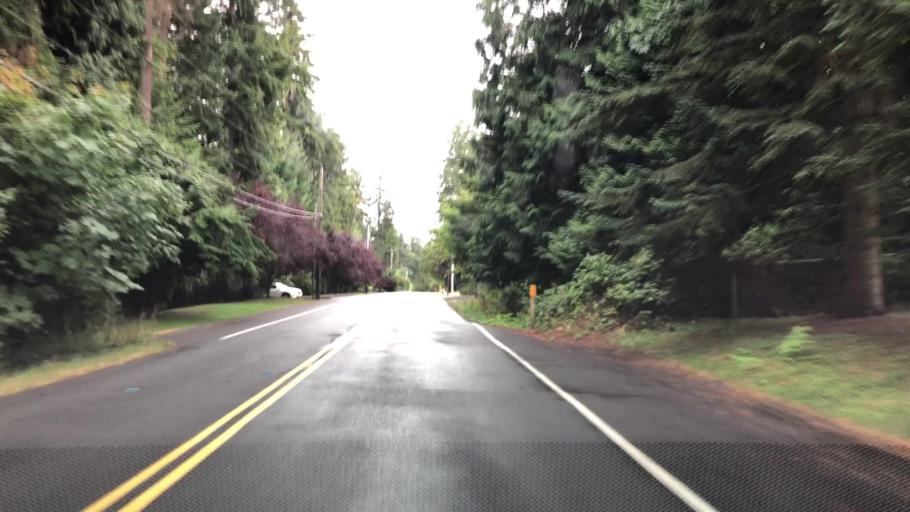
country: US
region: Washington
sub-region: King County
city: Woodinville
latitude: 47.7509
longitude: -122.1208
